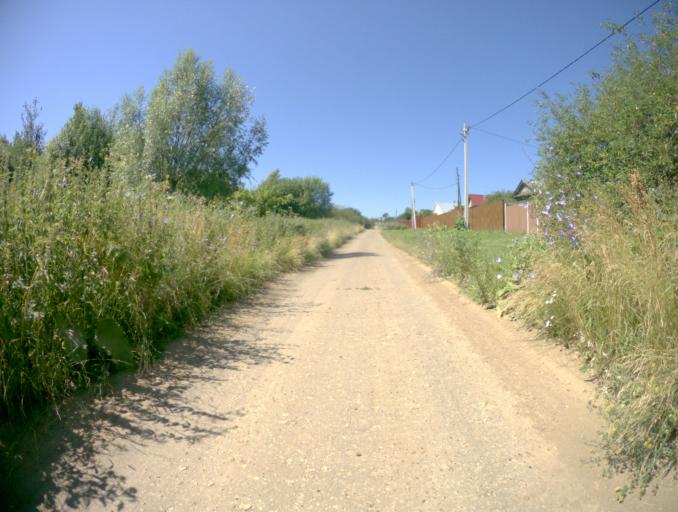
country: RU
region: Nizjnij Novgorod
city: Reshetikha
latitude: 56.1504
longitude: 43.3204
